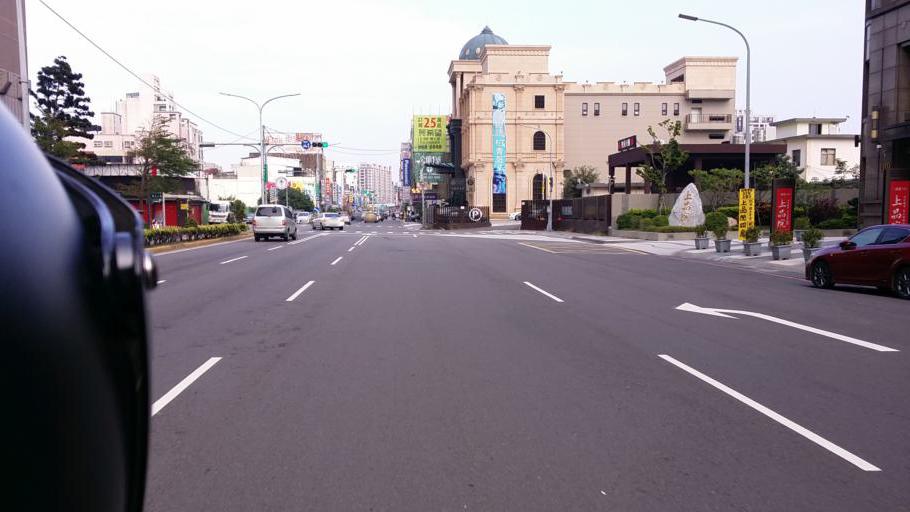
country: TW
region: Taiwan
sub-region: Hsinchu
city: Hsinchu
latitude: 24.8059
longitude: 120.9779
